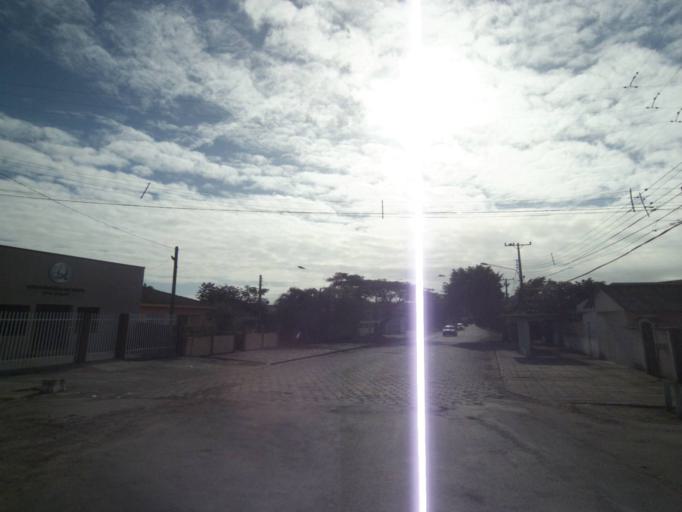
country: BR
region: Parana
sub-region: Paranagua
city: Paranagua
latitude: -25.5110
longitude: -48.5273
